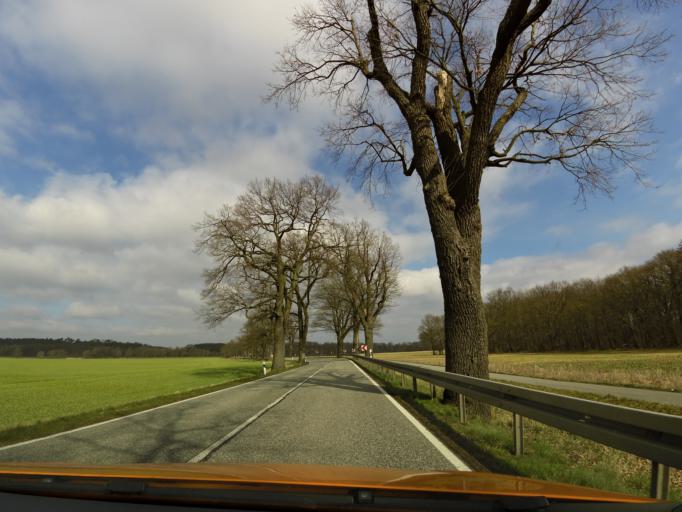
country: DE
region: Brandenburg
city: Rhinow
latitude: 52.6813
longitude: 12.3571
